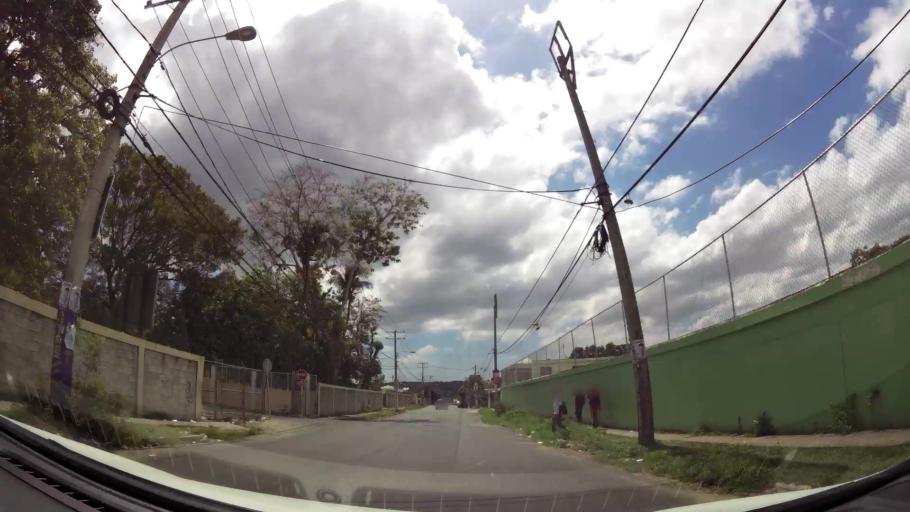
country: DO
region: San Cristobal
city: San Cristobal
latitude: 18.4103
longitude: -70.1138
